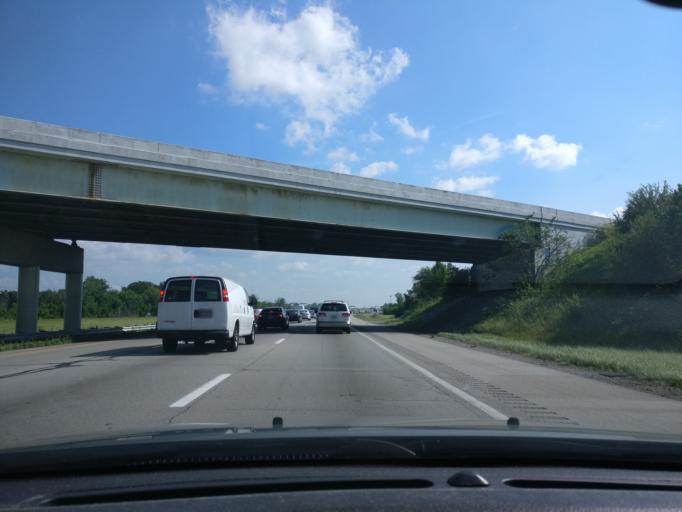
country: US
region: Ohio
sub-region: Montgomery County
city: West Carrollton City
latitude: 39.6230
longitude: -84.2306
